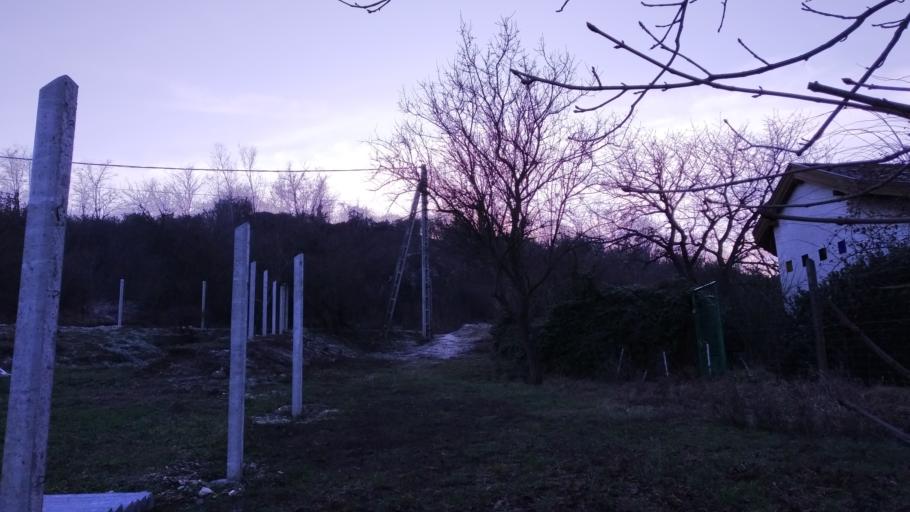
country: HU
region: Pest
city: Budakalasz
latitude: 47.6216
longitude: 19.0353
